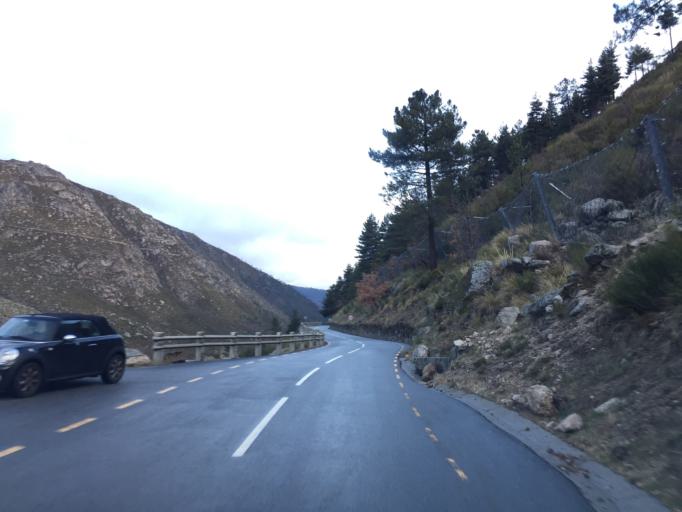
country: PT
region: Guarda
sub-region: Manteigas
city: Manteigas
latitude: 40.3473
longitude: -7.5612
